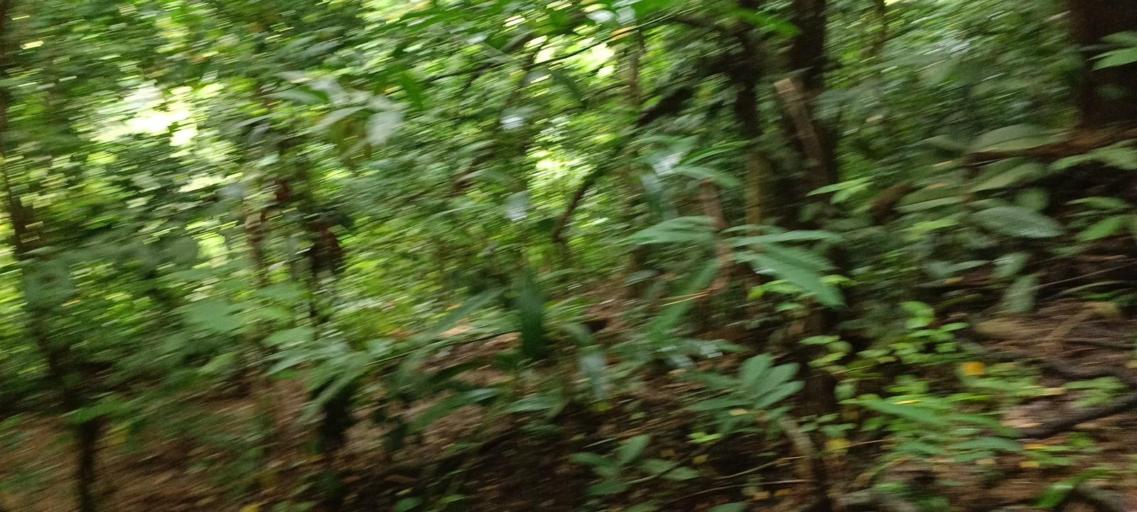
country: MY
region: Penang
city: Bukit Mertajam
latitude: 5.3581
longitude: 100.4911
